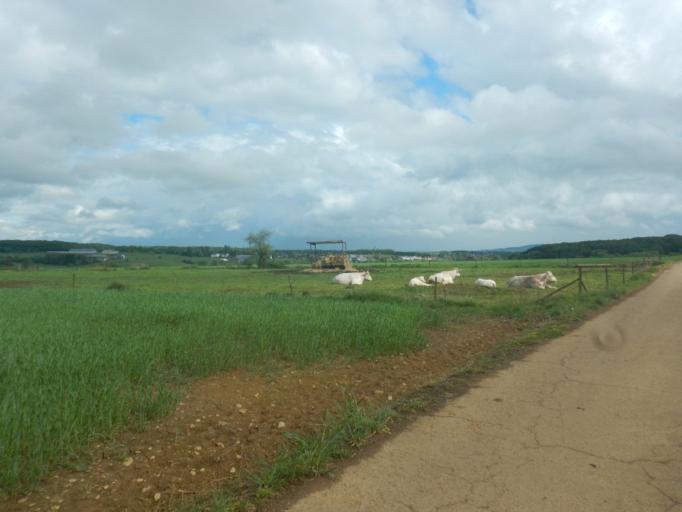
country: LU
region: Luxembourg
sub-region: Canton d'Esch-sur-Alzette
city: Reckange-sur-Mess
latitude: 49.5541
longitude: 6.0012
